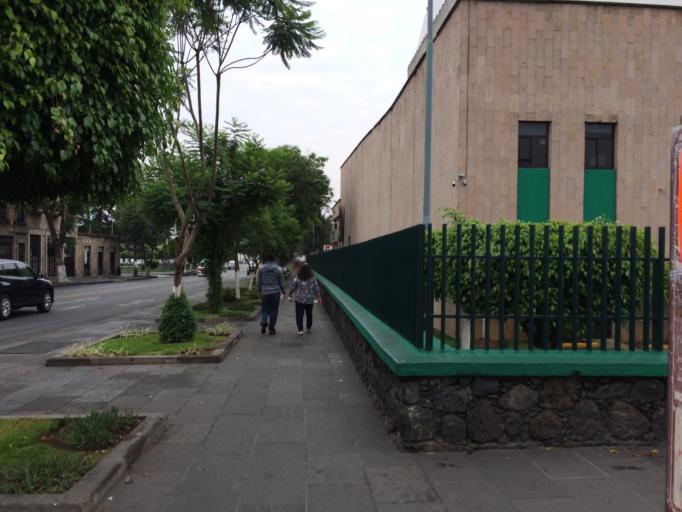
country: MX
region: Michoacan
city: Morelia
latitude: 19.7030
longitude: -101.2018
